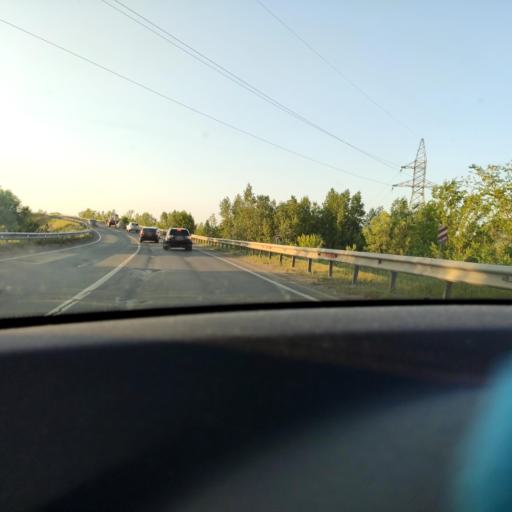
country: RU
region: Samara
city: Kinel'
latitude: 53.2489
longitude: 50.5910
